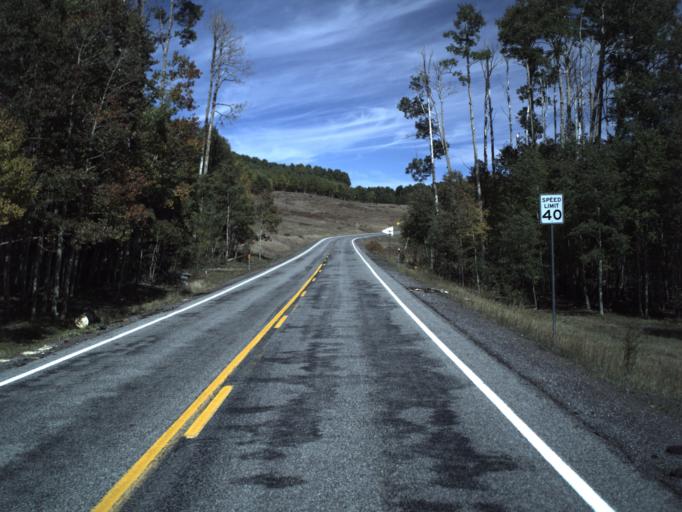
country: US
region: Utah
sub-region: Wayne County
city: Loa
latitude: 38.0490
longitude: -111.3289
